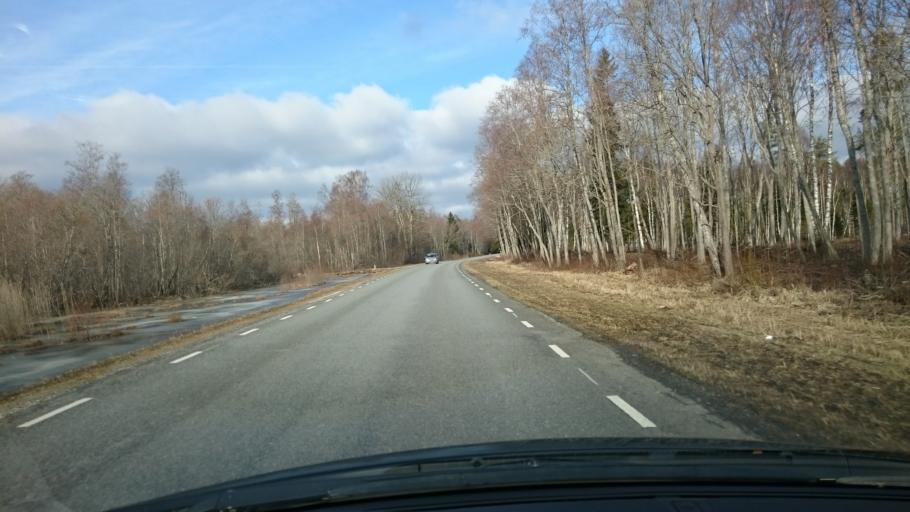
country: EE
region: Harju
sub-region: Keila linn
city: Keila
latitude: 59.3820
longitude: 24.3006
